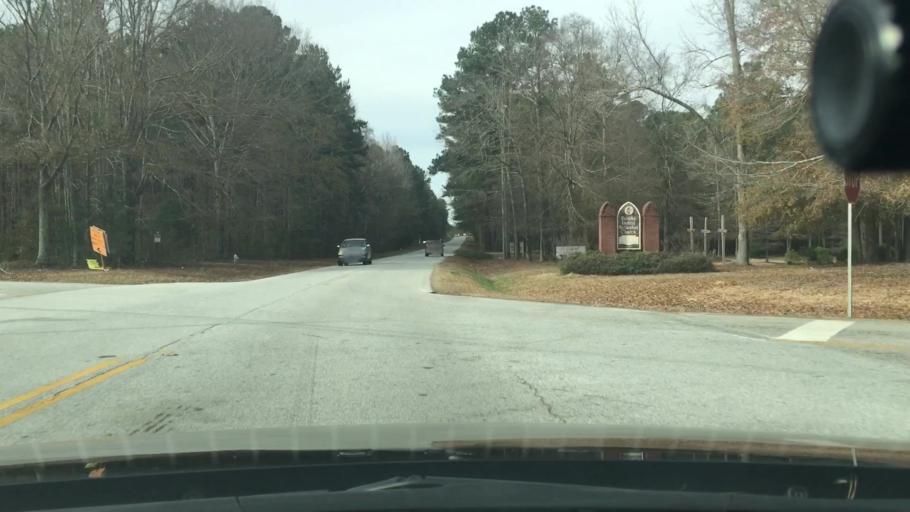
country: US
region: Georgia
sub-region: Coweta County
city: Senoia
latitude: 33.3054
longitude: -84.4670
